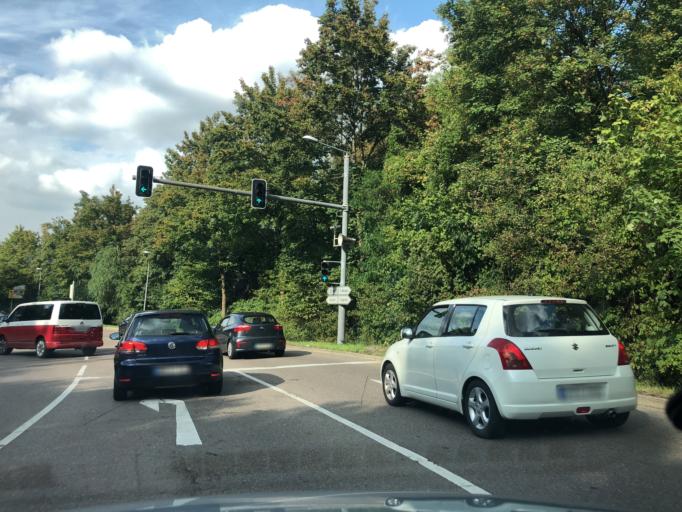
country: DE
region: Baden-Wuerttemberg
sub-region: Regierungsbezirk Stuttgart
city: Stuttgart
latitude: 48.7546
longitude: 9.1612
